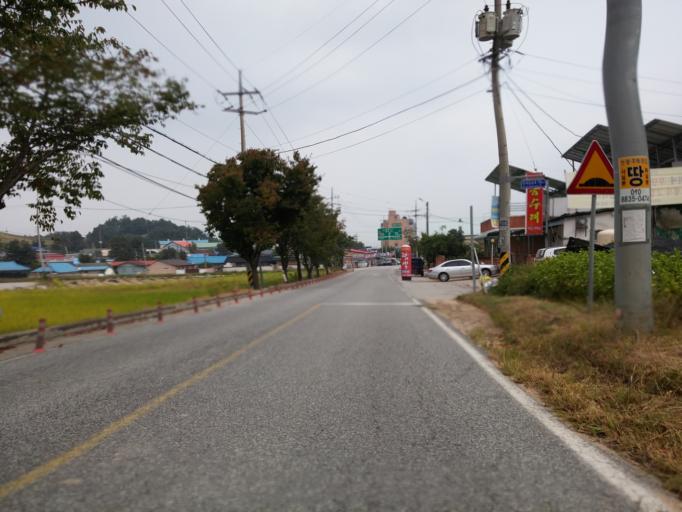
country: KR
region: Chungcheongbuk-do
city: Okcheon
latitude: 36.3961
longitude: 127.7298
